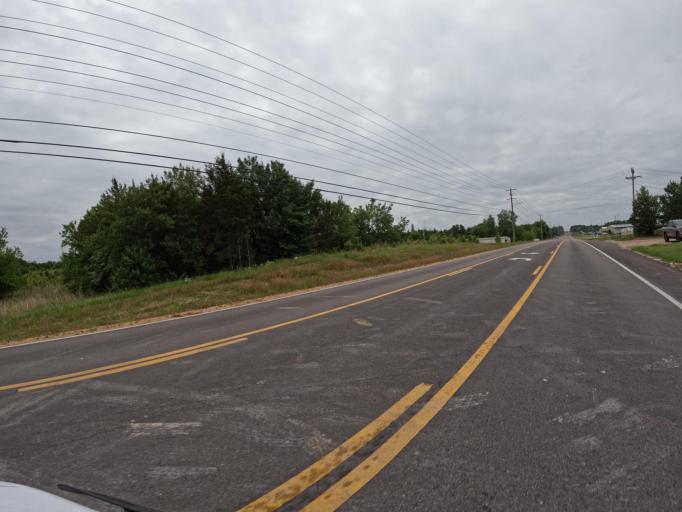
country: US
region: Mississippi
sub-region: Lee County
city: Tupelo
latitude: 34.2786
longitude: -88.7643
